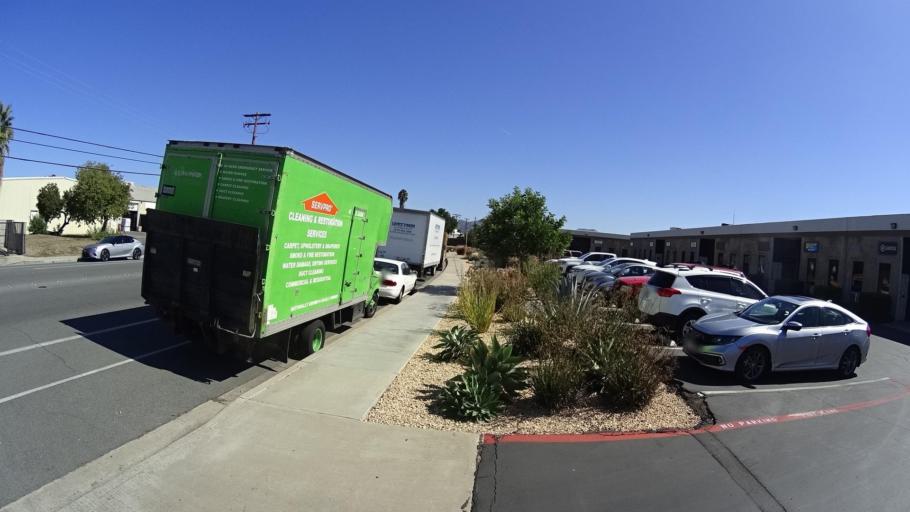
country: US
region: California
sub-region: San Diego County
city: El Cajon
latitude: 32.8122
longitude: -116.9672
